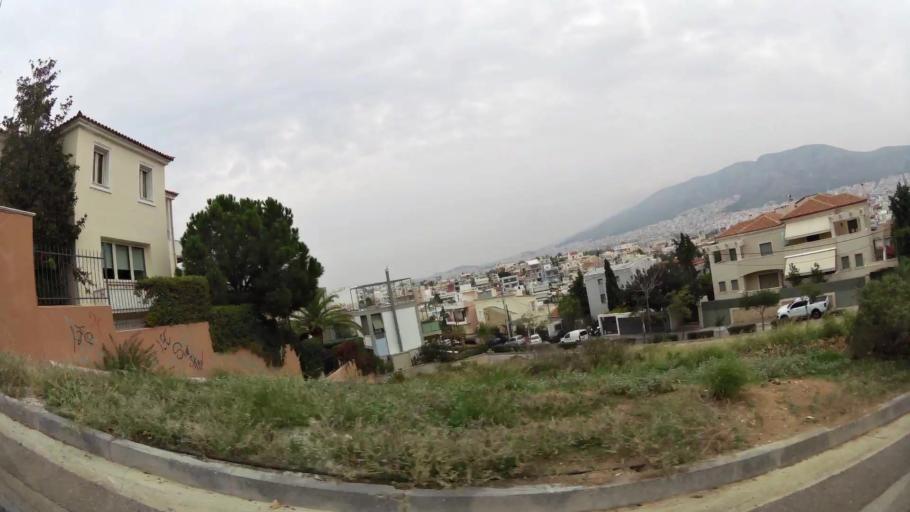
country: GR
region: Attica
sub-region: Nomarchia Athinas
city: Alimos
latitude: 37.9113
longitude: 23.7297
